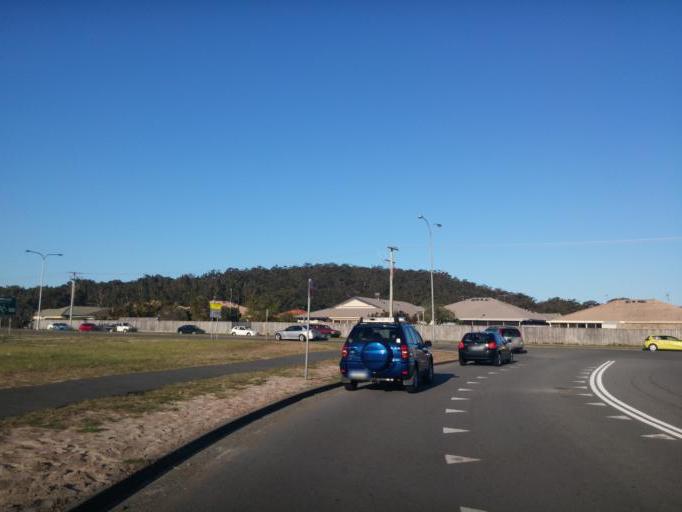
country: AU
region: New South Wales
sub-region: Port Stephens Shire
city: Corlette
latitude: -32.7356
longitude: 152.1088
